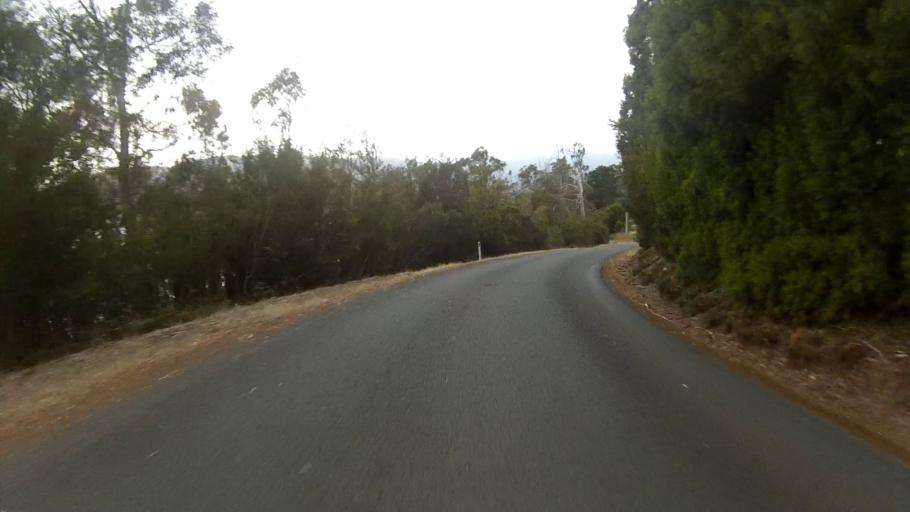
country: AU
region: Tasmania
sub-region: Huon Valley
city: Cygnet
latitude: -43.2150
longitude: 147.1057
